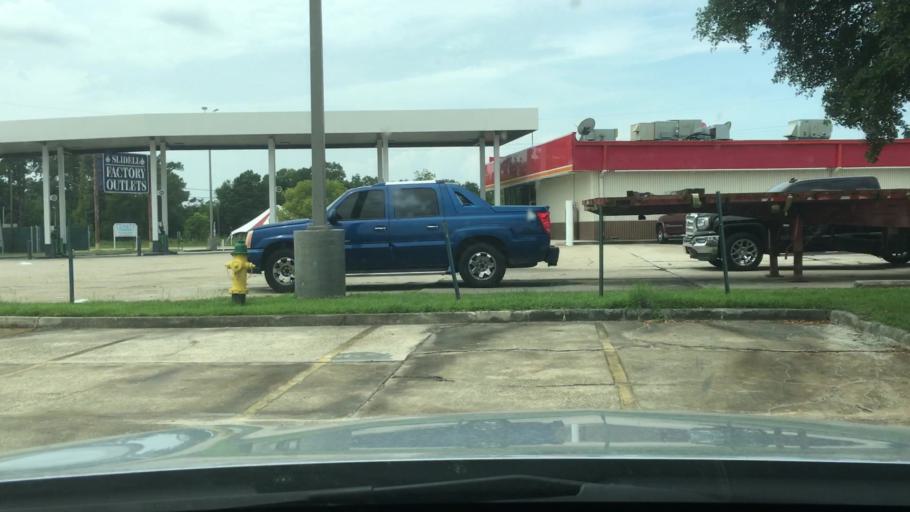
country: US
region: Louisiana
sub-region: Saint Tammany Parish
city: Slidell
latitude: 30.2464
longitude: -89.7605
